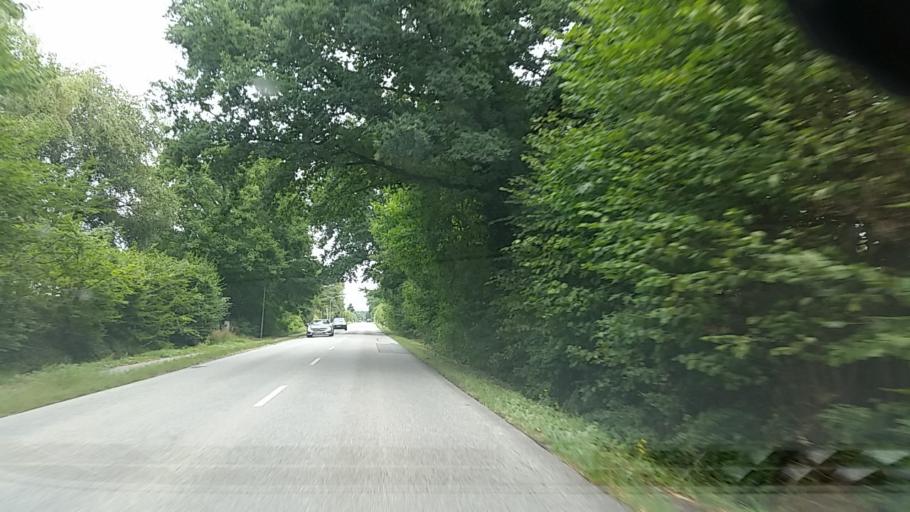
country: DE
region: Schleswig-Holstein
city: Hohenhorn
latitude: 53.4949
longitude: 10.3638
